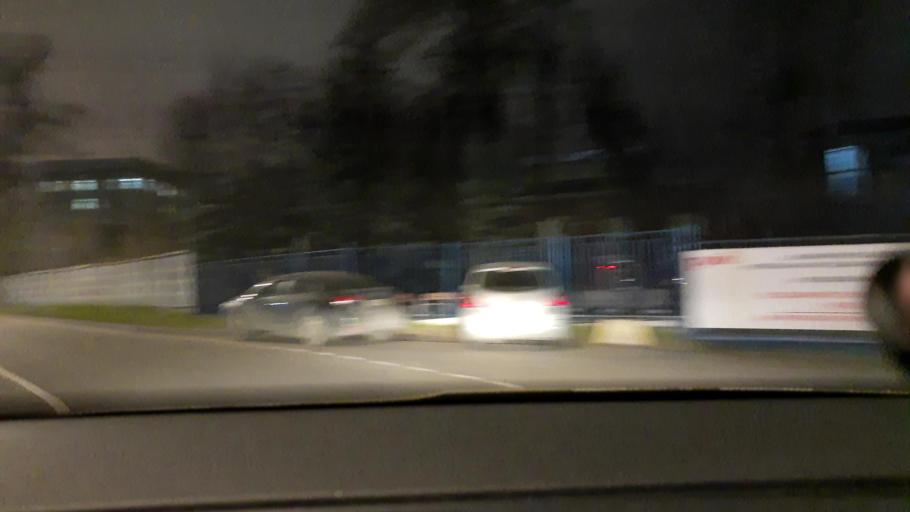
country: RU
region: Moscow
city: Sokol'niki
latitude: 55.7985
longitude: 37.6446
